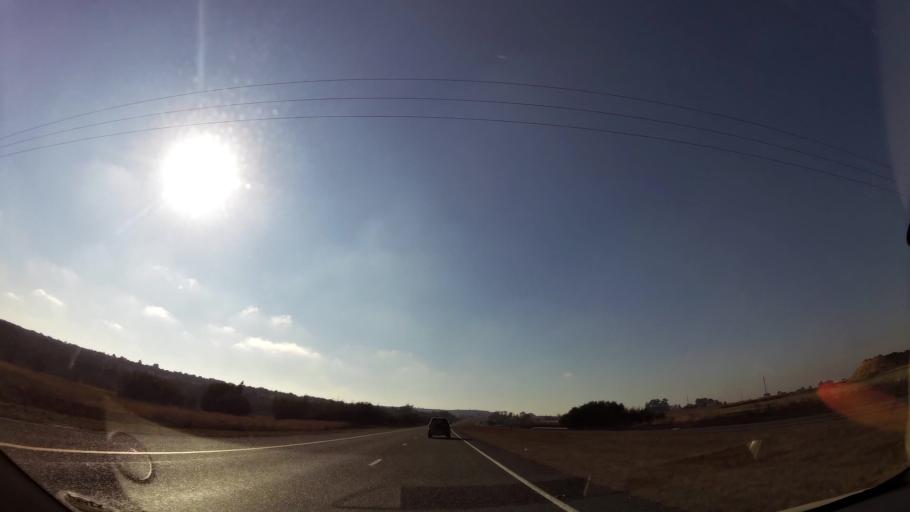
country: ZA
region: Gauteng
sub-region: City of Tshwane Metropolitan Municipality
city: Bronkhorstspruit
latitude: -26.0171
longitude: 28.9450
